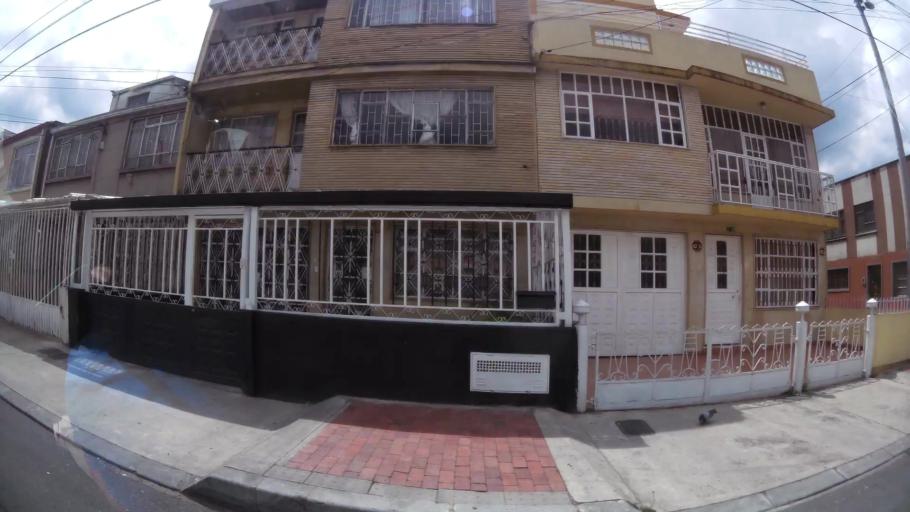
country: CO
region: Bogota D.C.
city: Bogota
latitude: 4.6000
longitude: -74.0983
